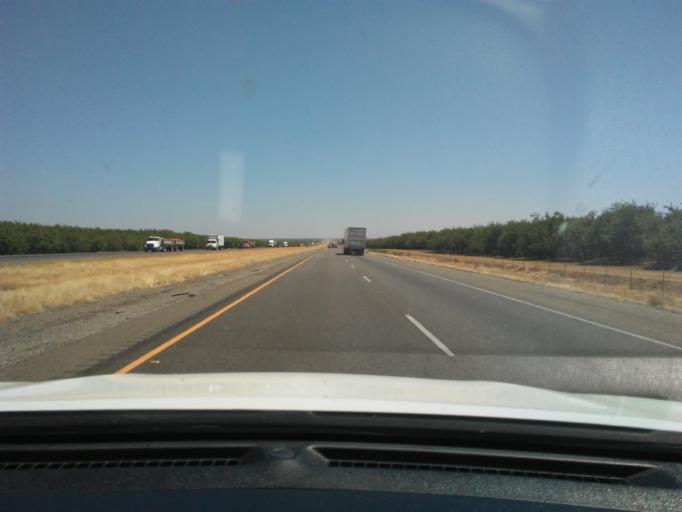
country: US
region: California
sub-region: Merced County
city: South Dos Palos
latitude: 36.8307
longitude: -120.7607
